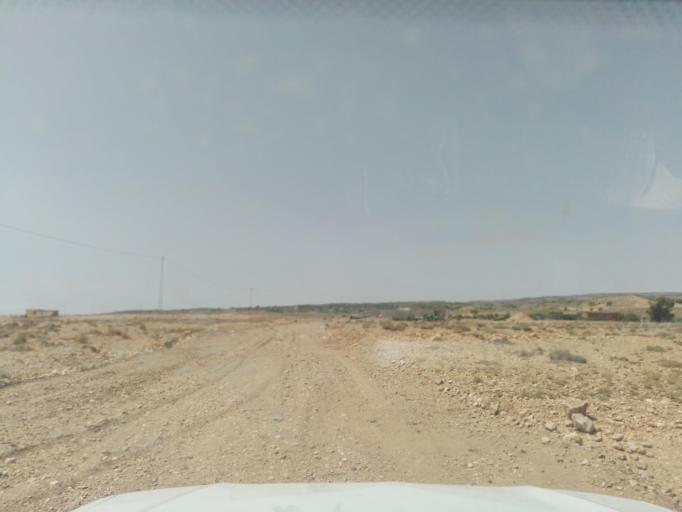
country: TN
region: Al Qasrayn
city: Kasserine
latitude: 35.2865
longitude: 8.9268
